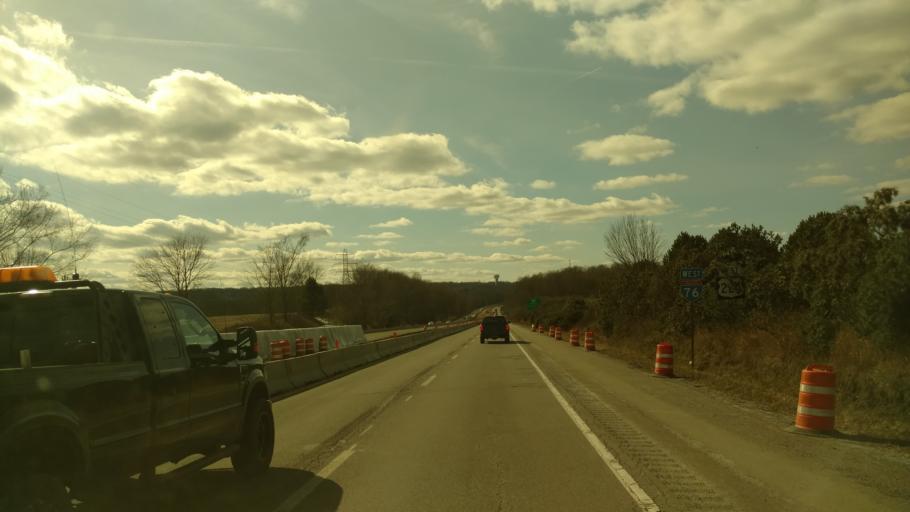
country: US
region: Ohio
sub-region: Summit County
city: Norton
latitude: 41.0401
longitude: -81.6695
